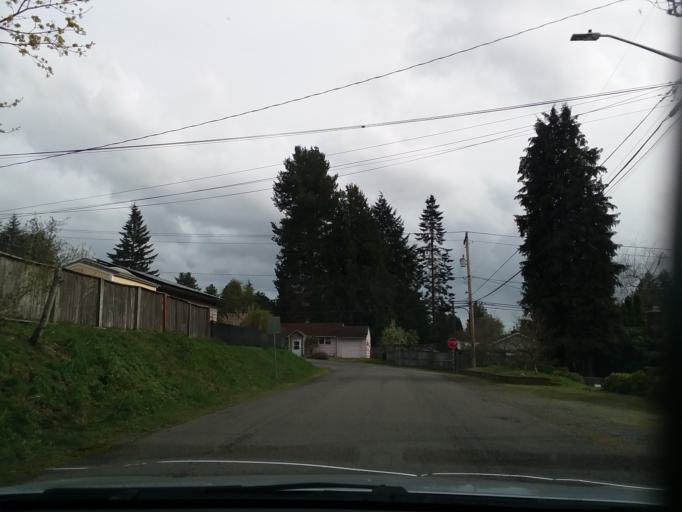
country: US
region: Washington
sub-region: King County
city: Shoreline
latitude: 47.7526
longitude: -122.3160
